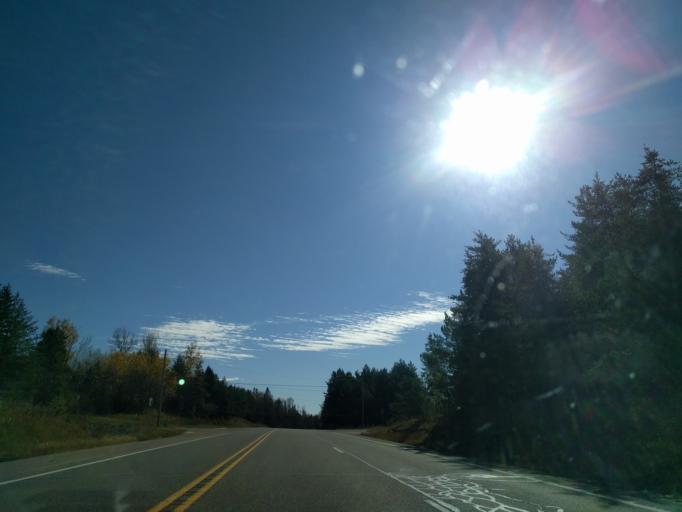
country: US
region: Michigan
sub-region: Marquette County
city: West Ishpeming
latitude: 46.4949
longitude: -87.9195
